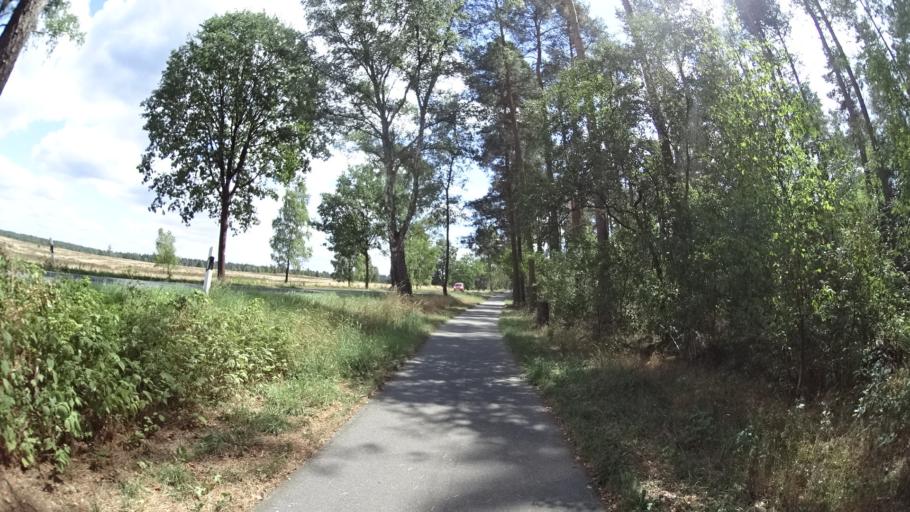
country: DE
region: Lower Saxony
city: Undeloh
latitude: 53.2199
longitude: 9.9388
